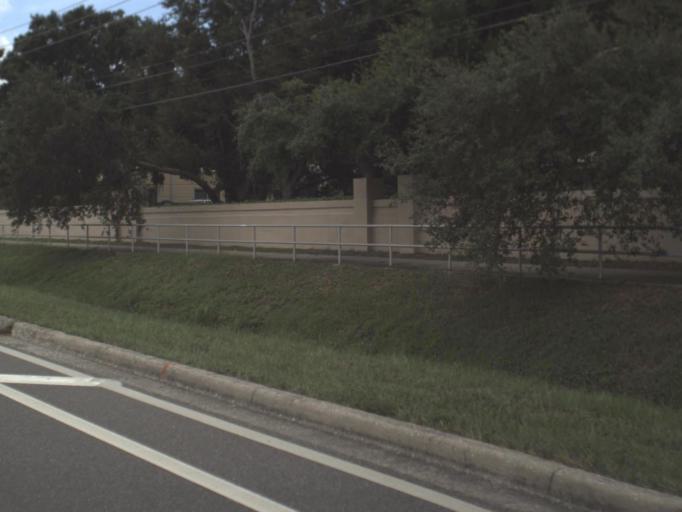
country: US
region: Florida
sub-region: Pinellas County
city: Saint George
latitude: 28.0422
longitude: -82.7092
